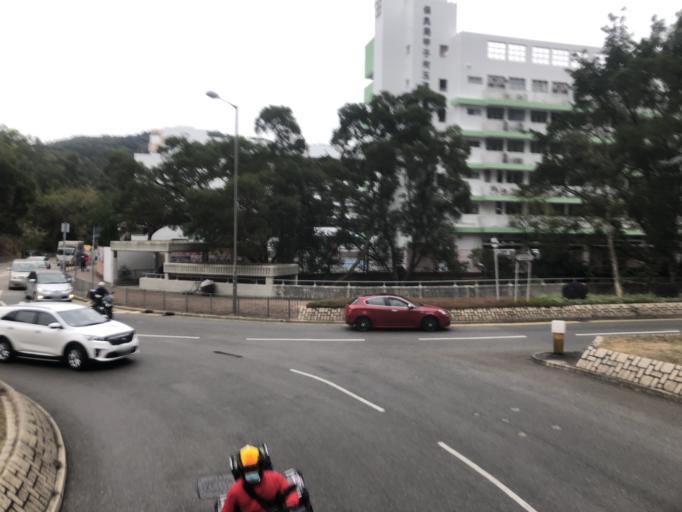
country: HK
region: Sai Kung
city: Sai Kung
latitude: 22.3191
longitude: 114.2657
